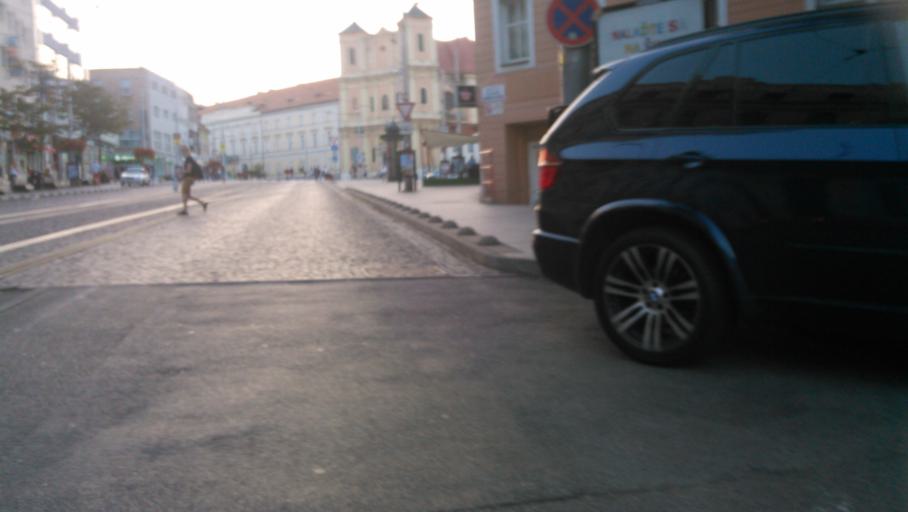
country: SK
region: Bratislavsky
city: Bratislava
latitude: 48.1457
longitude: 17.1087
